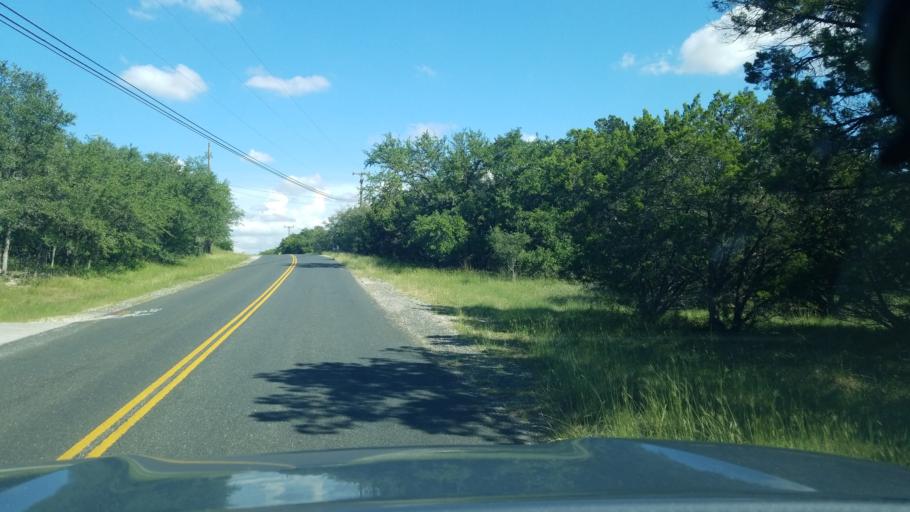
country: US
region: Texas
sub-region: Bexar County
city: Timberwood Park
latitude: 29.6765
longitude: -98.5009
